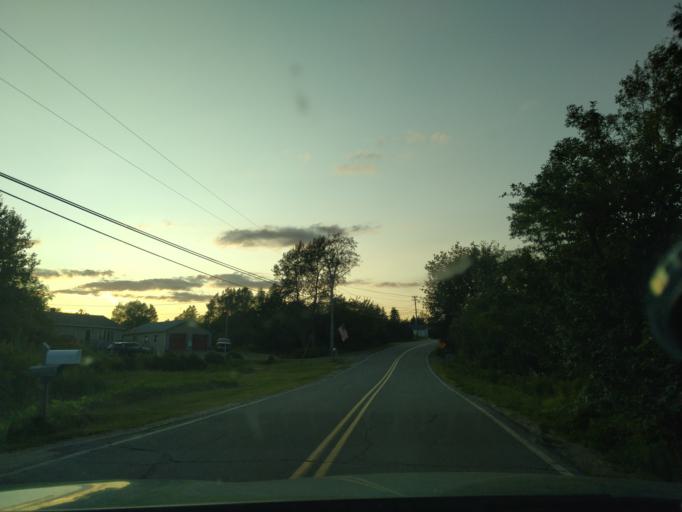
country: US
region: Maine
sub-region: Hancock County
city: Gouldsboro
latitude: 44.3858
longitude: -68.0385
